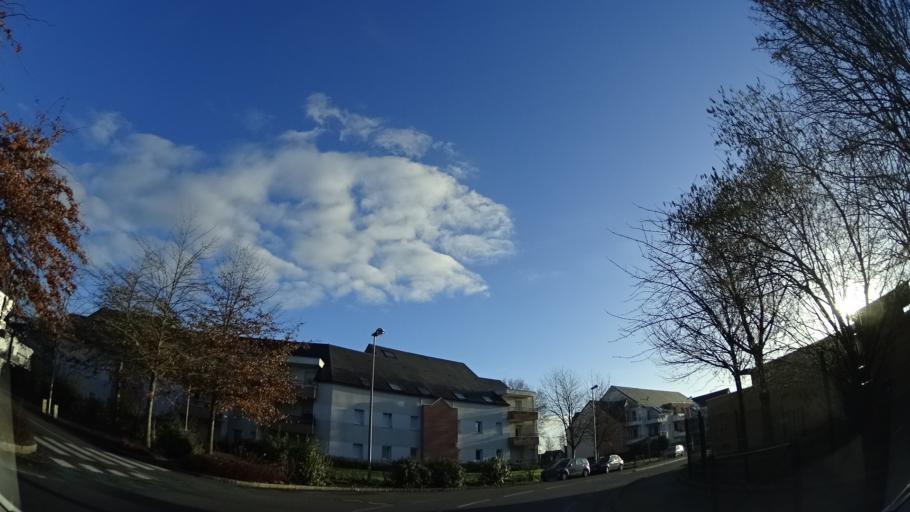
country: FR
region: Brittany
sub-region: Departement d'Ille-et-Vilaine
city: Betton
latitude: 48.1851
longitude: -1.6493
